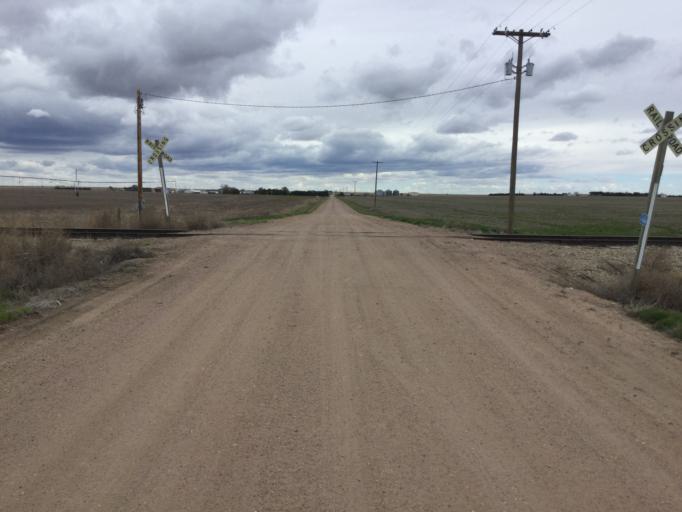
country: US
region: Kansas
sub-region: Sherman County
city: Goodland
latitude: 39.3403
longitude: -101.7447
